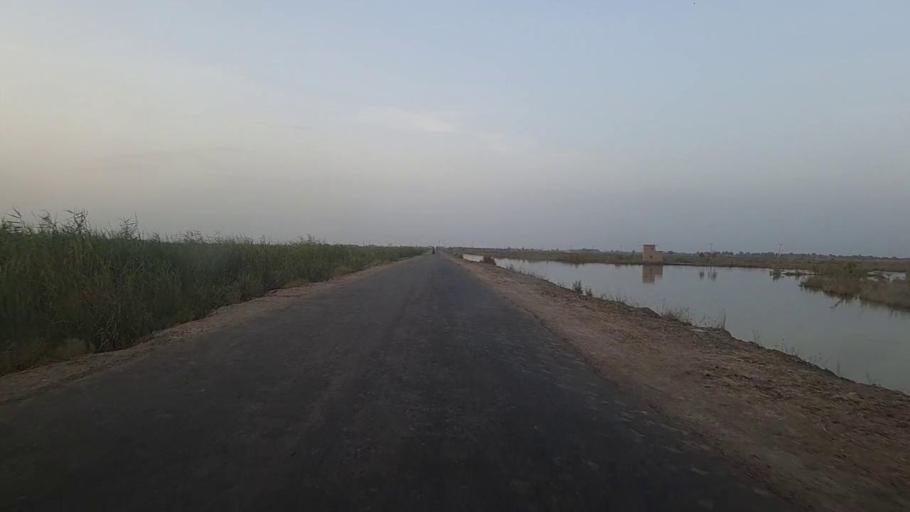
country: PK
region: Sindh
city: Radhan
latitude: 27.1484
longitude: 67.9376
